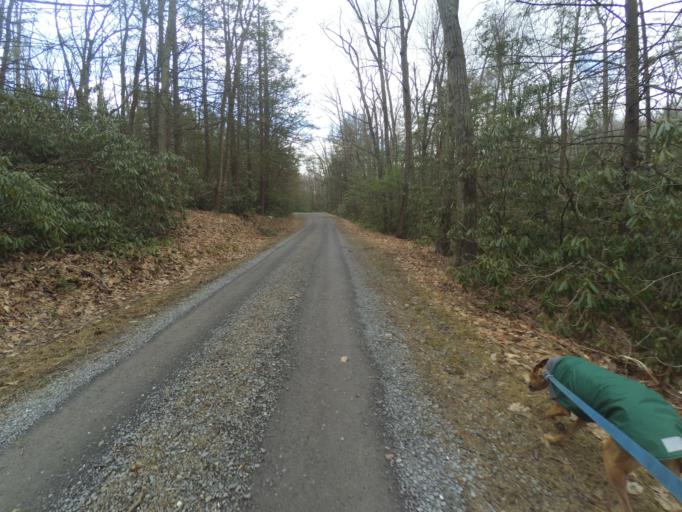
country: US
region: Pennsylvania
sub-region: Centre County
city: Boalsburg
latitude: 40.7479
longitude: -77.7136
